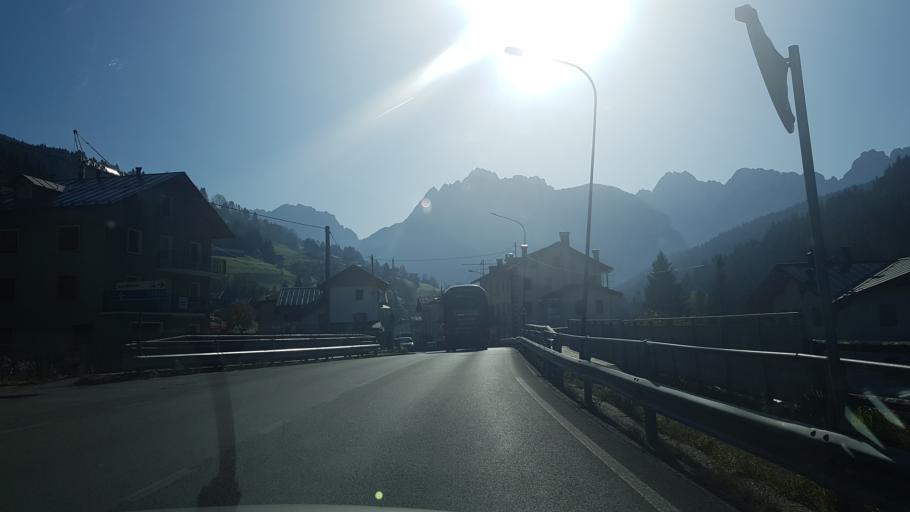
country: IT
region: Veneto
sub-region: Provincia di Belluno
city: San Nicolo Comelico
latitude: 46.5783
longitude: 12.5297
